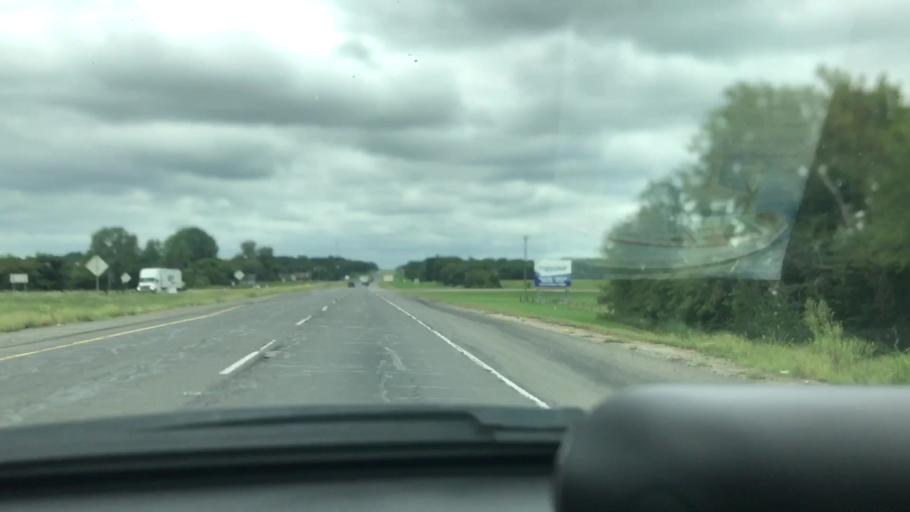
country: US
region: Oklahoma
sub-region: Muskogee County
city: Muskogee
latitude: 35.8115
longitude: -95.4022
